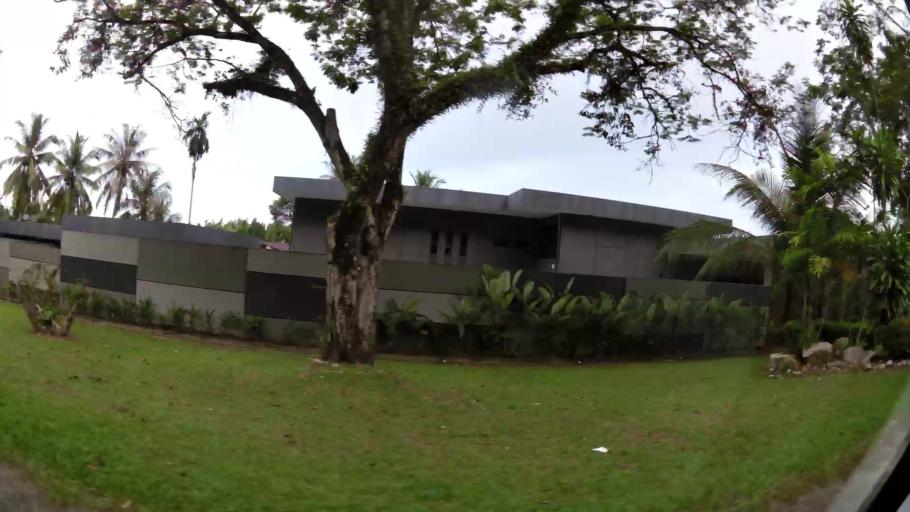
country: BN
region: Brunei and Muara
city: Bandar Seri Begawan
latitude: 4.9211
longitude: 115.0089
